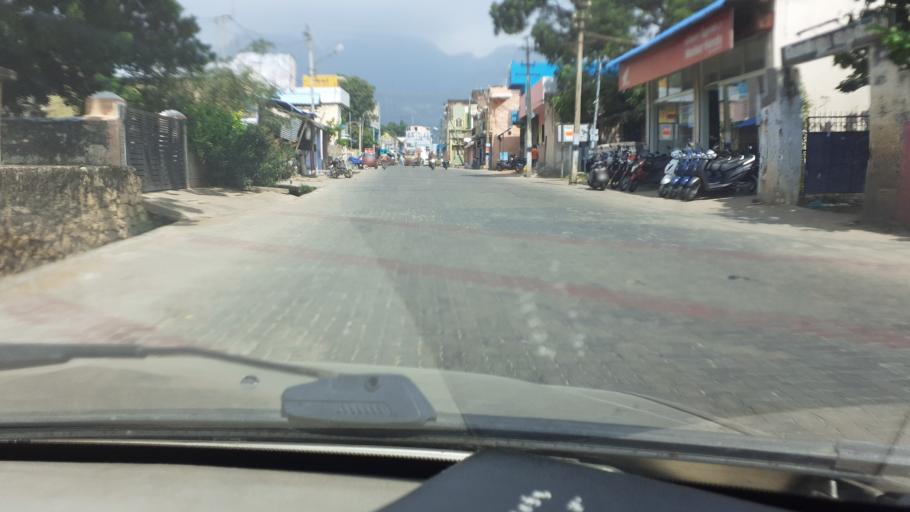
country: IN
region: Tamil Nadu
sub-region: Kanniyakumari
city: Suchindram
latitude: 8.2483
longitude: 77.5212
